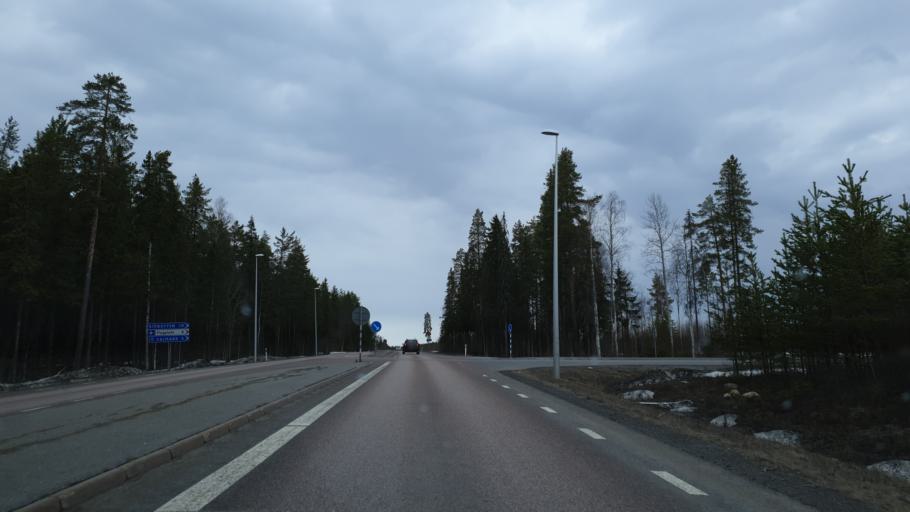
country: SE
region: Vaesterbotten
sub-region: Skelleftea Kommun
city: Viken
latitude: 64.6649
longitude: 20.9509
